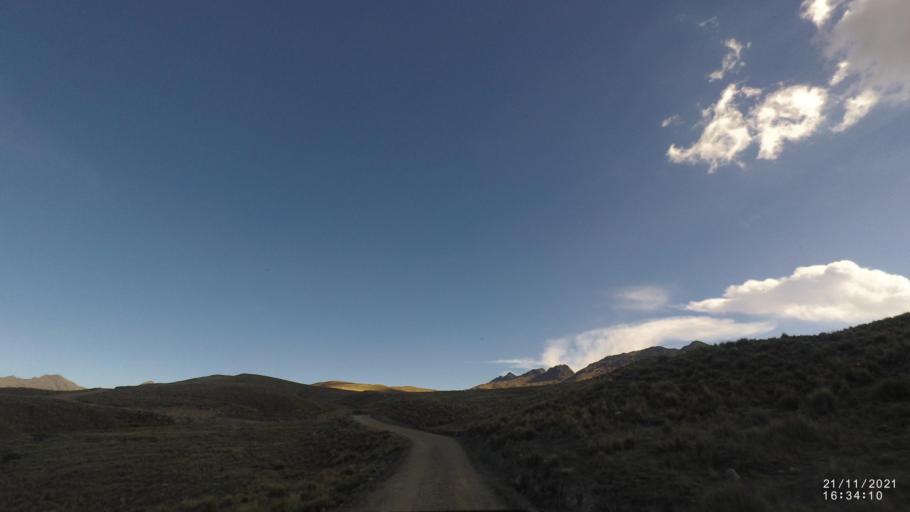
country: BO
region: Cochabamba
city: Cochabamba
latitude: -17.0349
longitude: -66.2794
